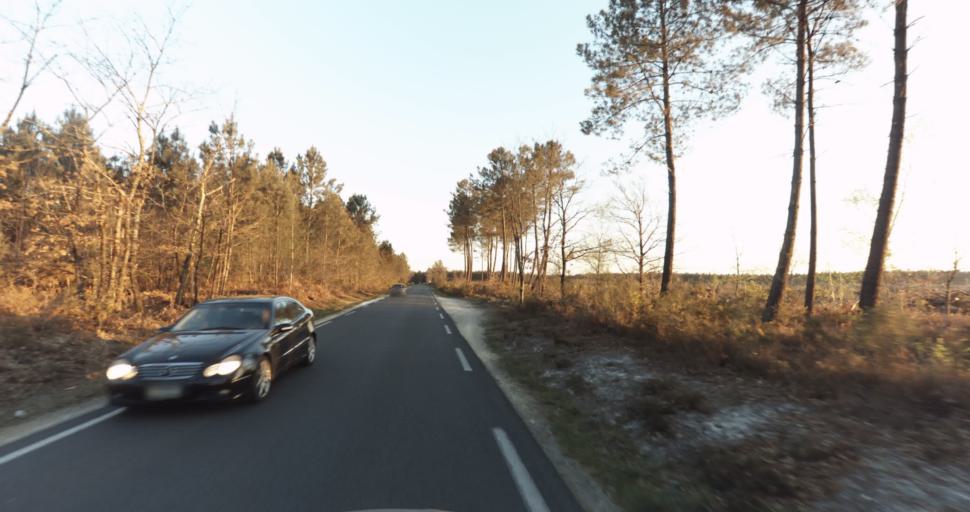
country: FR
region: Aquitaine
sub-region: Departement de la Gironde
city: Martignas-sur-Jalle
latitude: 44.8229
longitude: -0.7574
